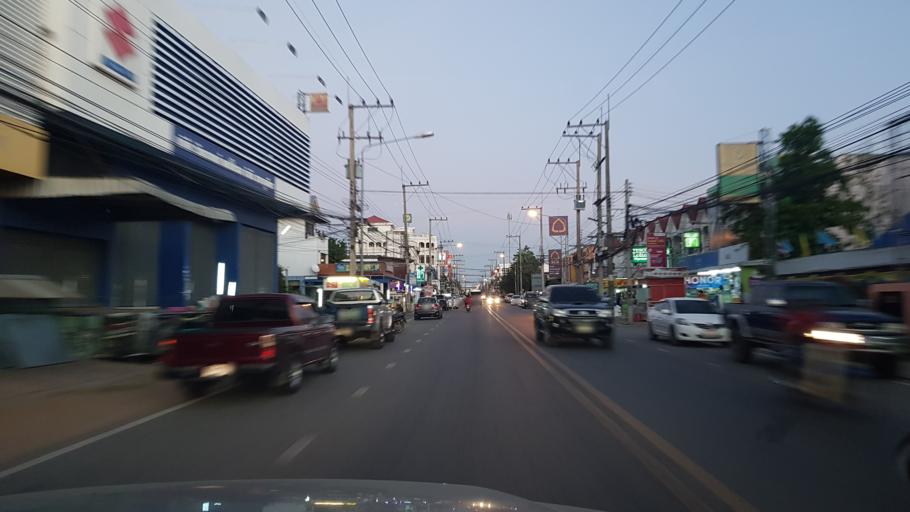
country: TH
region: Chaiyaphum
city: Phu Khiao
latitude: 16.3666
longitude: 102.1331
